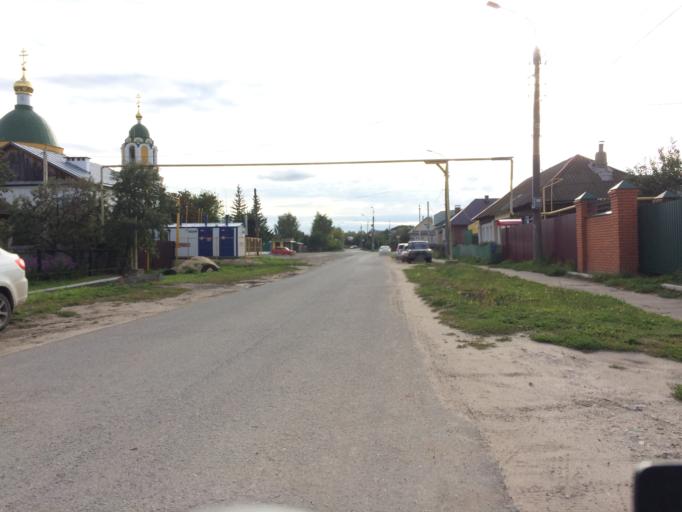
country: RU
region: Mariy-El
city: Yoshkar-Ola
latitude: 56.6512
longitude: 47.9818
